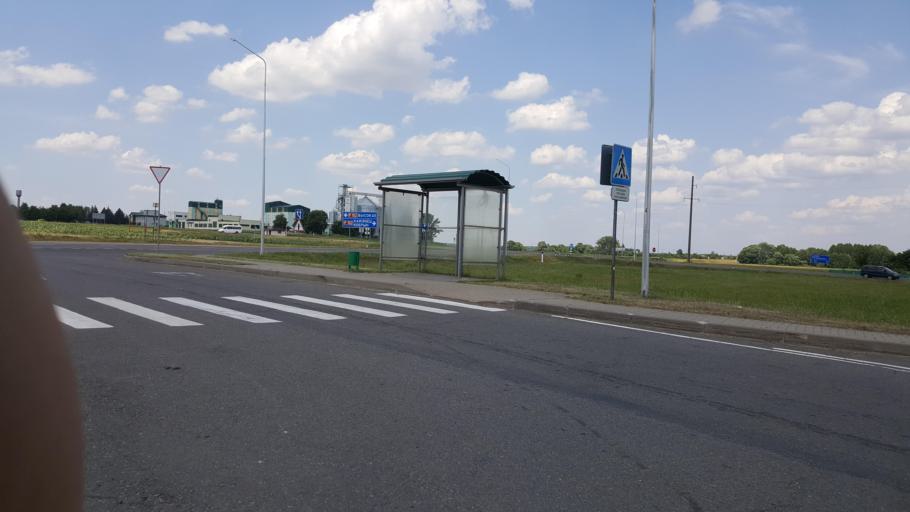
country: BY
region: Brest
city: Kamyanyets
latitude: 52.3977
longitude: 23.7858
